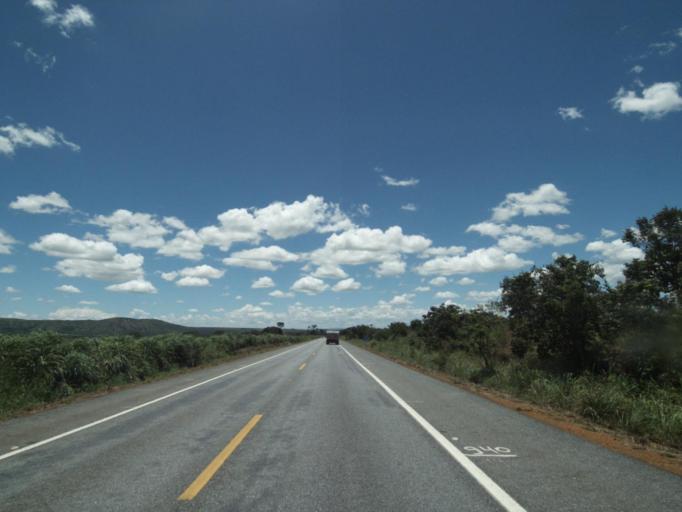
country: BR
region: Goias
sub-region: Pirenopolis
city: Pirenopolis
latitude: -15.5152
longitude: -48.6230
